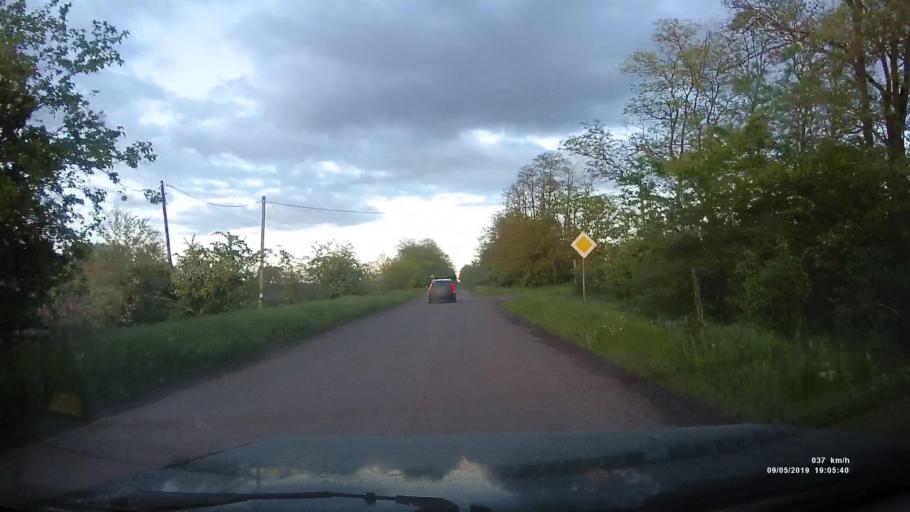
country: RU
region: Krasnodarskiy
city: Kanelovskaya
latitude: 46.7384
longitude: 39.1831
